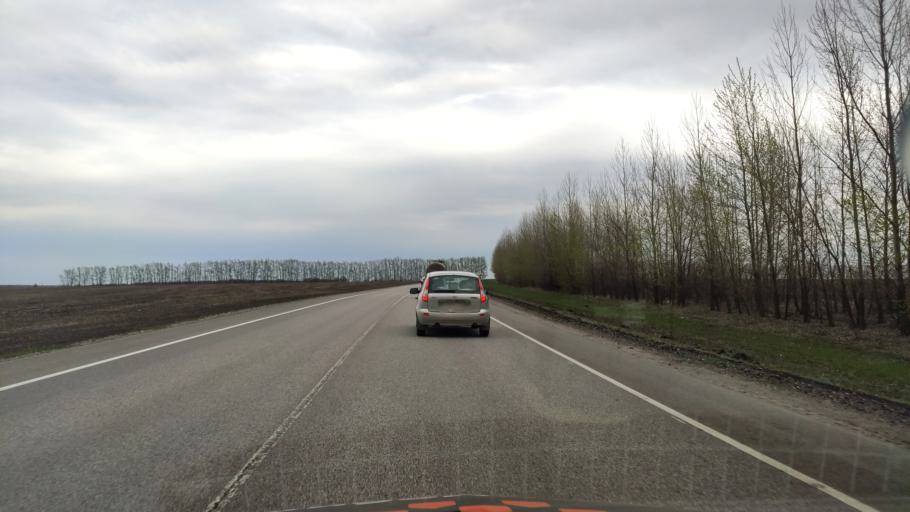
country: RU
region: Voronezj
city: Nizhnedevitsk
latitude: 51.5845
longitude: 38.5039
